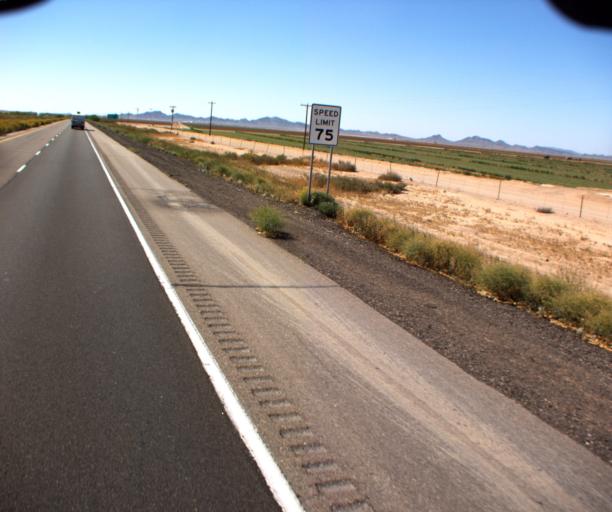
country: US
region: Arizona
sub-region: Maricopa County
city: Gila Bend
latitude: 32.9195
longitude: -112.9005
